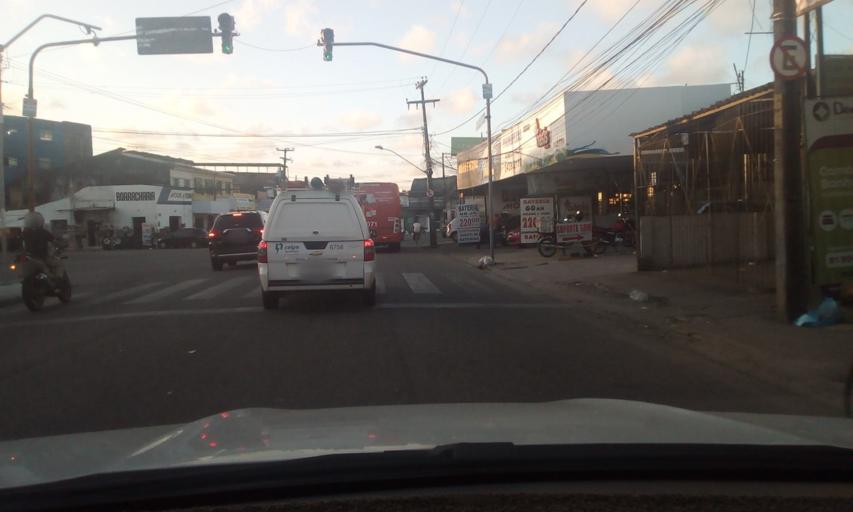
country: BR
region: Pernambuco
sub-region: Recife
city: Recife
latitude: -8.0763
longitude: -34.9070
